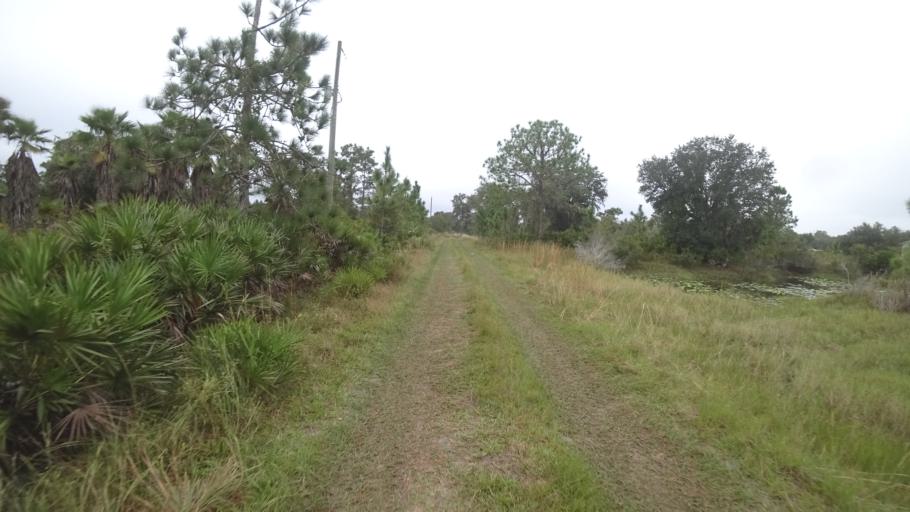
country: US
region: Florida
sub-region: Sarasota County
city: Warm Mineral Springs
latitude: 27.2758
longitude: -82.1252
